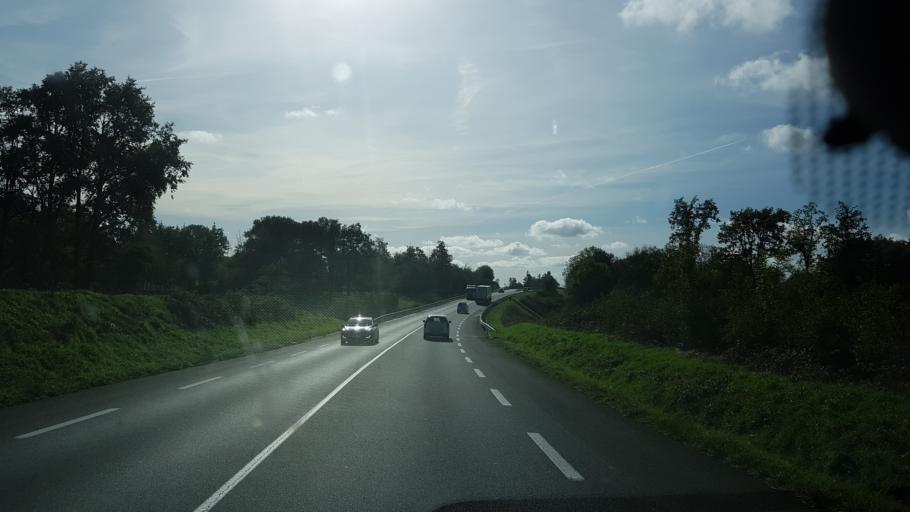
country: FR
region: Poitou-Charentes
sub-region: Departement de la Charente
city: Saint-Claud
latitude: 45.9096
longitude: 0.4908
